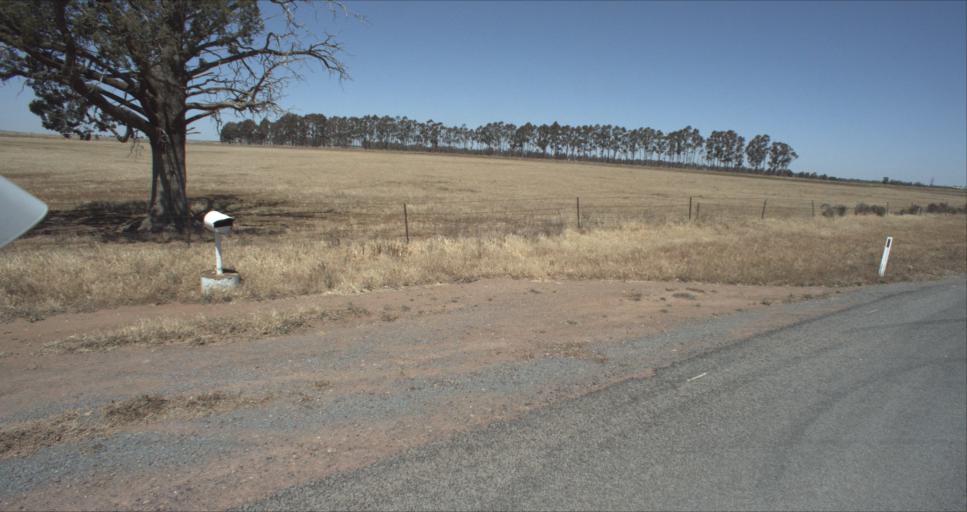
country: AU
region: New South Wales
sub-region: Leeton
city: Leeton
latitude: -34.5338
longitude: 146.4467
